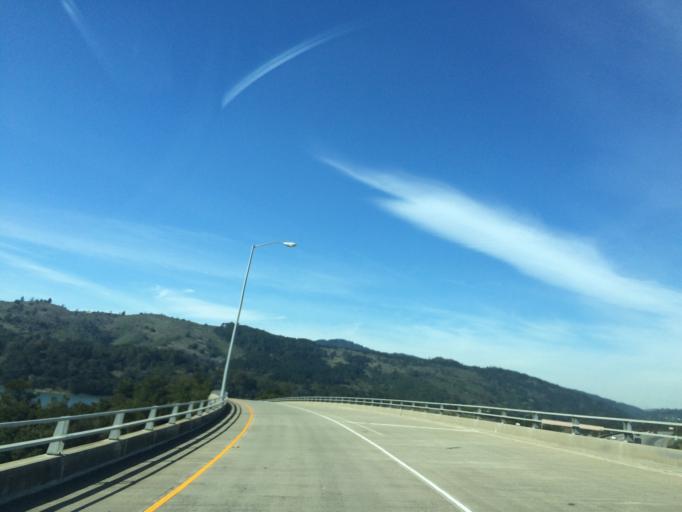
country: US
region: California
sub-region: San Mateo County
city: Highlands-Baywood Park
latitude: 37.5077
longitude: -122.3389
